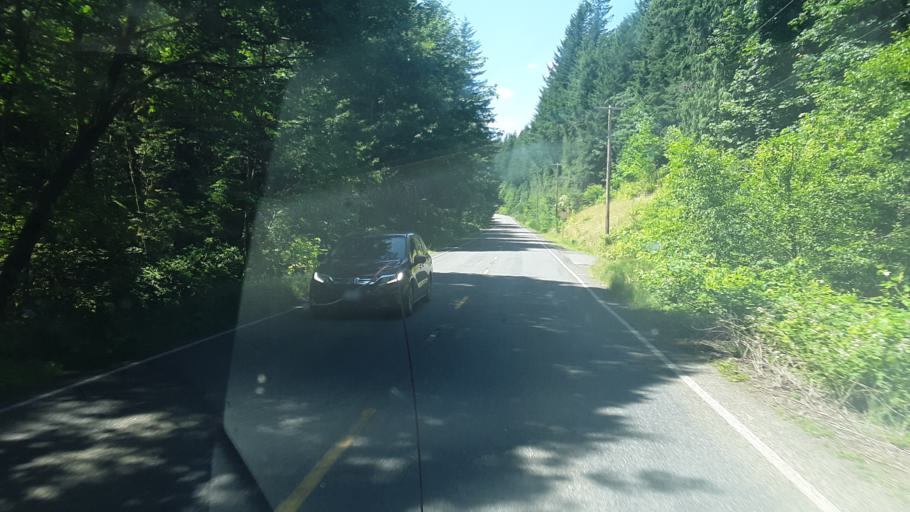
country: US
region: Washington
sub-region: Clark County
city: Amboy
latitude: 46.0569
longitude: -122.2940
